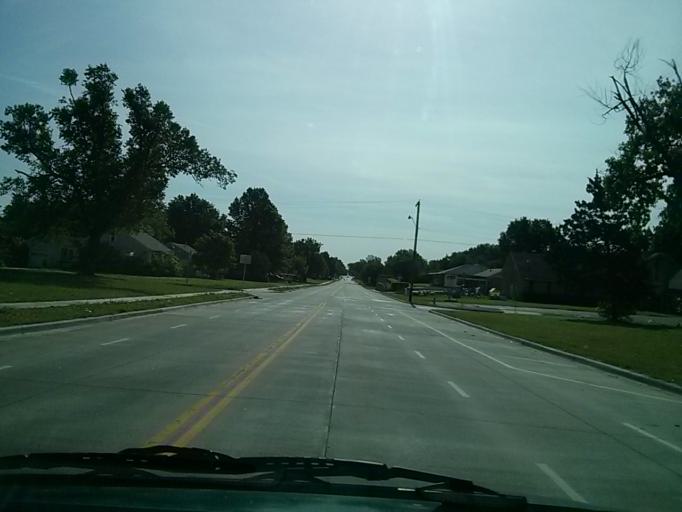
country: US
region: Oklahoma
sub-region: Tulsa County
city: Tulsa
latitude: 36.1551
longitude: -95.9143
